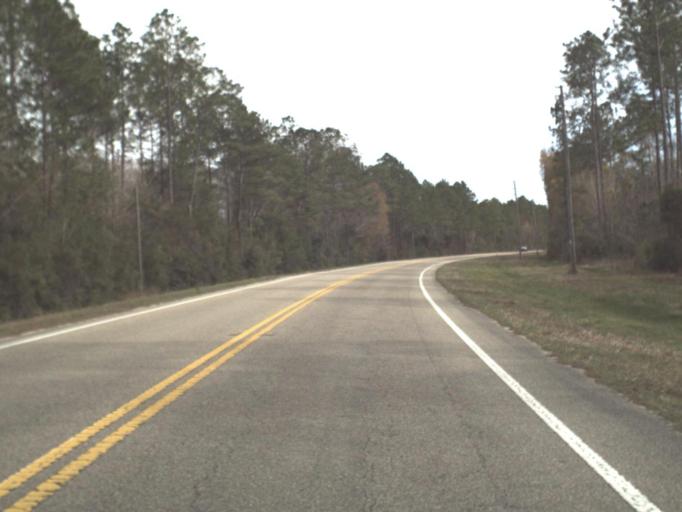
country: US
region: Florida
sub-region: Leon County
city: Woodville
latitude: 30.2229
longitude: -84.2030
